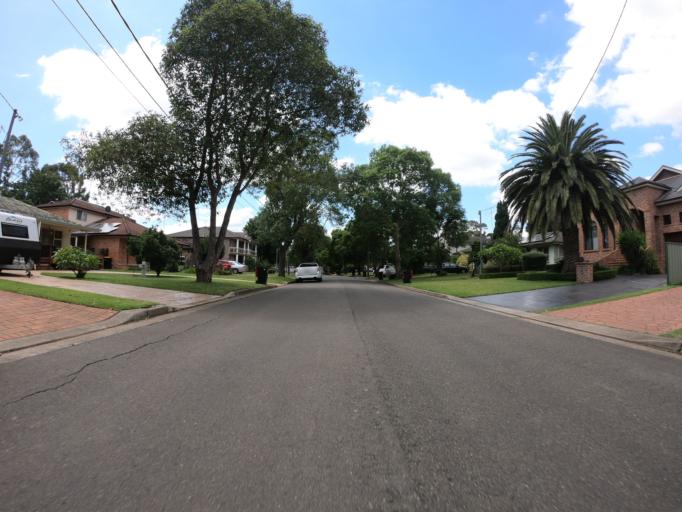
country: AU
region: New South Wales
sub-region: Penrith Municipality
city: Penrith
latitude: -33.7521
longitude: 150.6799
